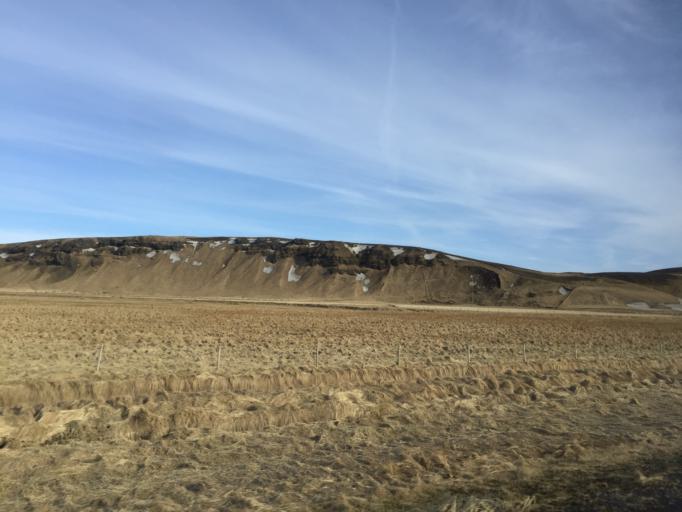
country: IS
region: South
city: Vestmannaeyjar
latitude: 63.4434
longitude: -19.1999
